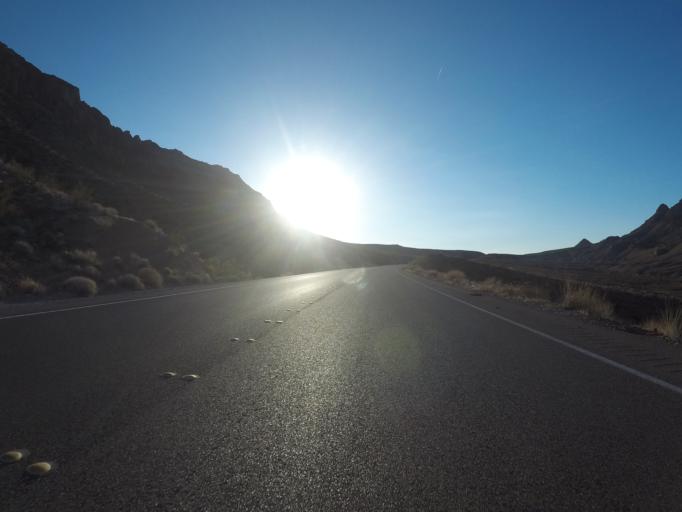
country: US
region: Nevada
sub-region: Clark County
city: Moapa Valley
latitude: 36.2452
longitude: -114.4944
